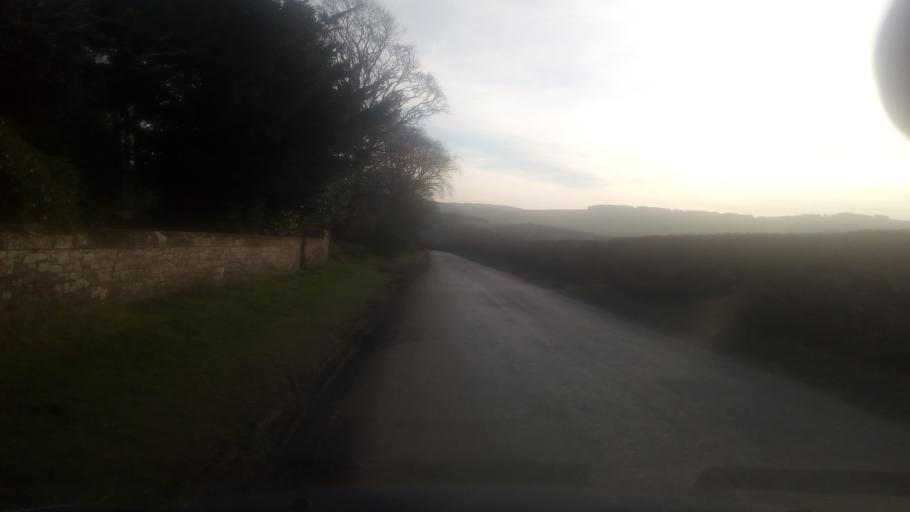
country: GB
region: Scotland
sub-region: The Scottish Borders
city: Jedburgh
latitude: 55.3907
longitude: -2.5952
